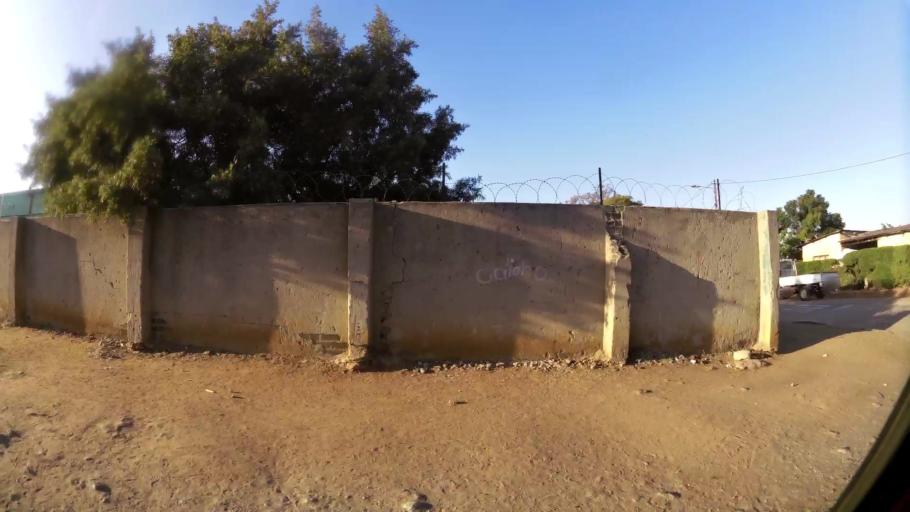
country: ZA
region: North-West
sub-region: Bojanala Platinum District Municipality
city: Rustenburg
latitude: -25.6413
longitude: 27.2190
